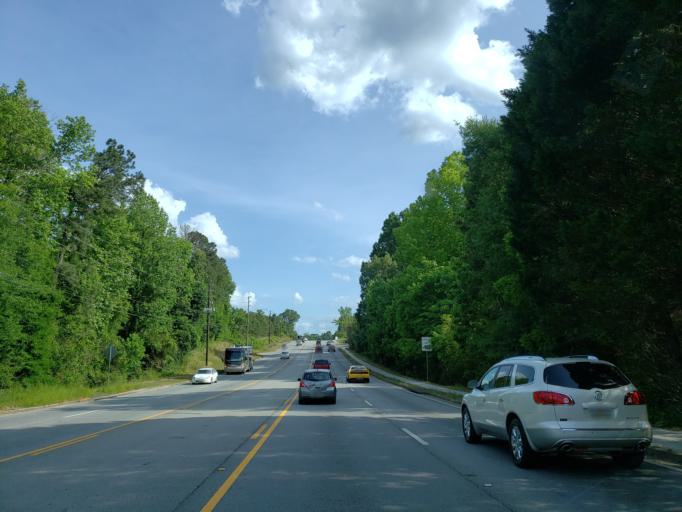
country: US
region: Georgia
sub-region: Carroll County
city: Carrollton
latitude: 33.5892
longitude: -85.0789
